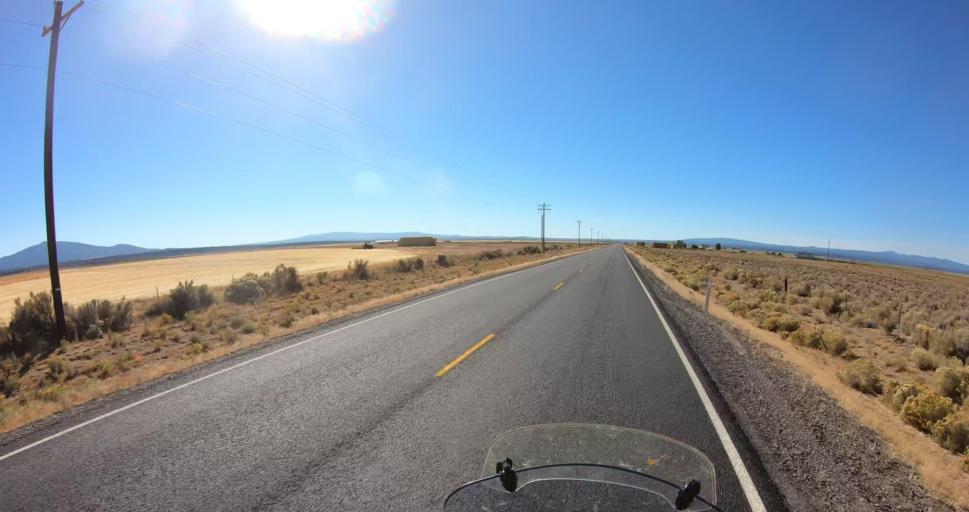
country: US
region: Oregon
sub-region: Deschutes County
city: La Pine
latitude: 43.1285
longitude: -120.9702
